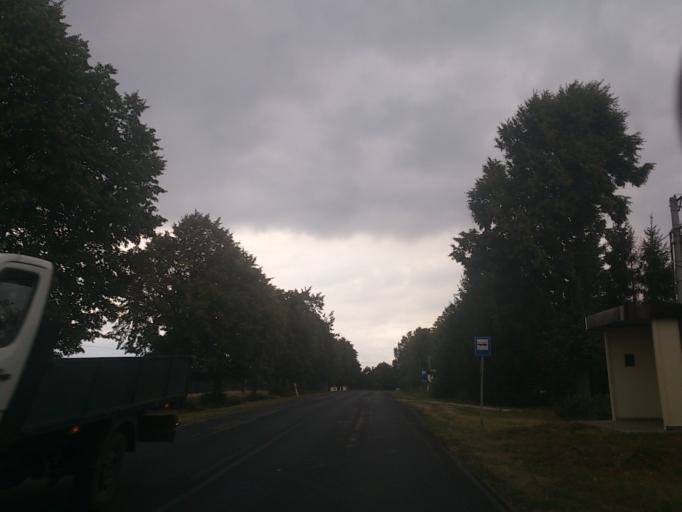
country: PL
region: Kujawsko-Pomorskie
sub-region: Powiat golubsko-dobrzynski
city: Golub-Dobrzyn
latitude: 53.0728
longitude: 19.0654
